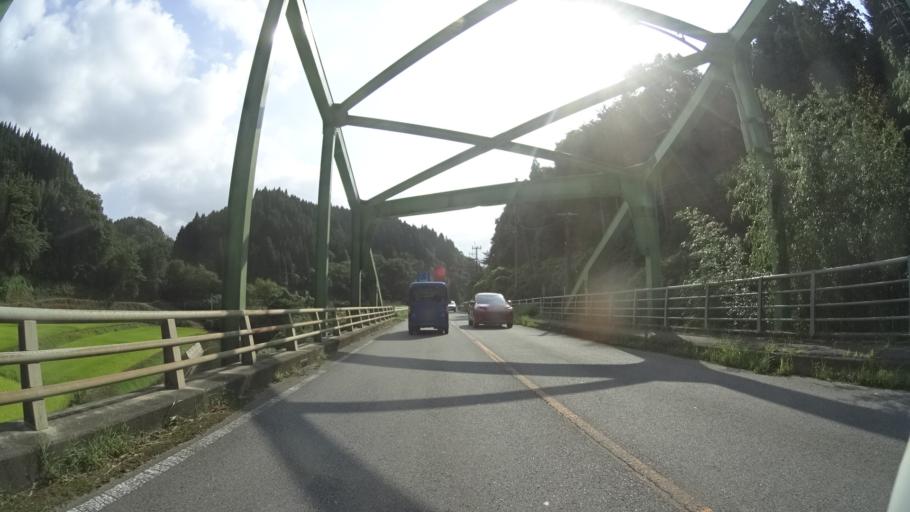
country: JP
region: Kumamoto
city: Aso
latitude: 32.6856
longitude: 131.0599
